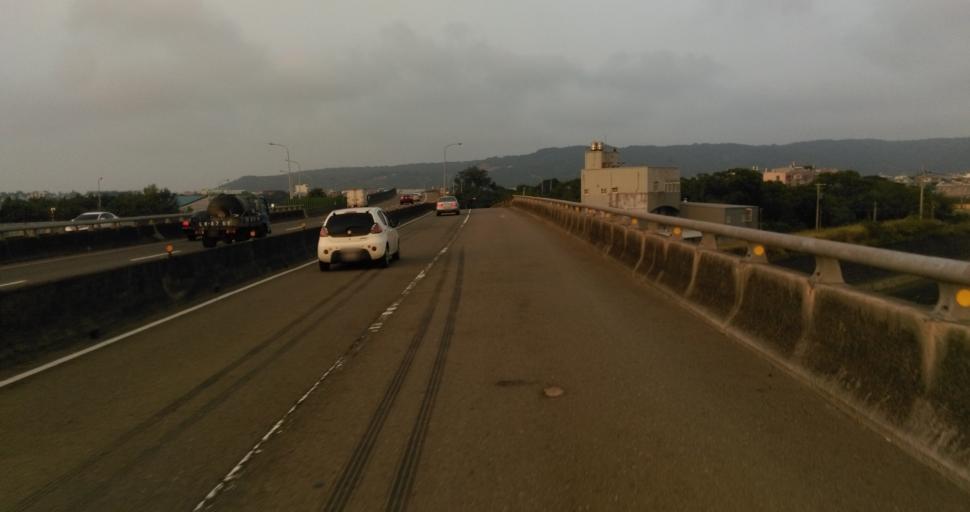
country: TW
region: Taiwan
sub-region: Hsinchu
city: Hsinchu
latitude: 24.8597
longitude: 120.9504
